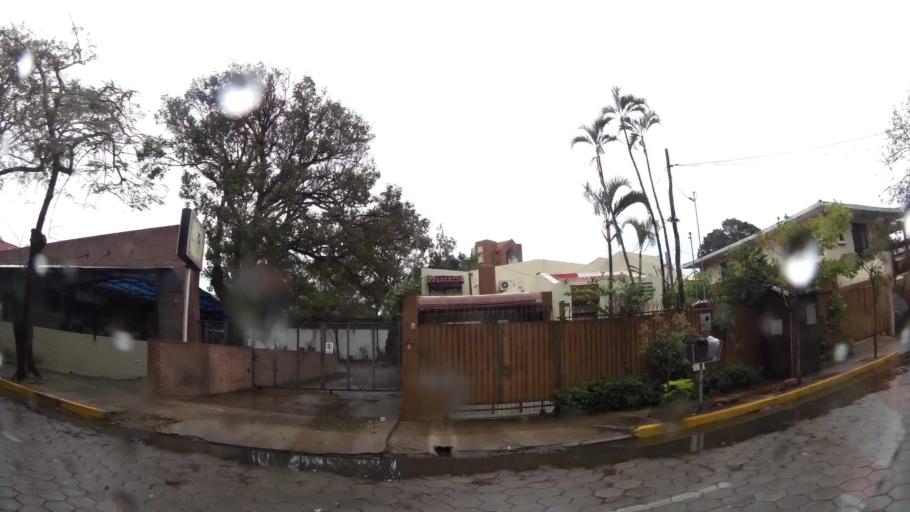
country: BO
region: Santa Cruz
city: Santa Cruz de la Sierra
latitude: -17.7965
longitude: -63.1799
